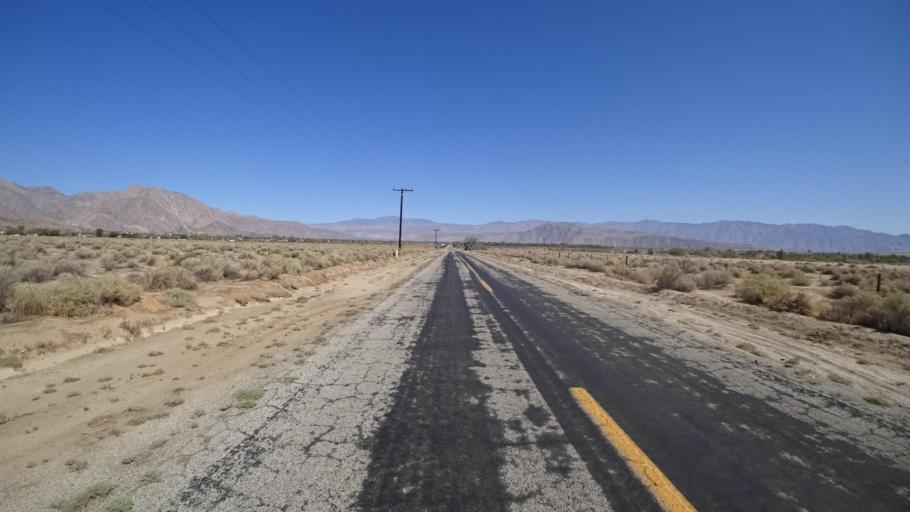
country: US
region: California
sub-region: San Diego County
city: Borrego Springs
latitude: 33.2405
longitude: -116.3656
